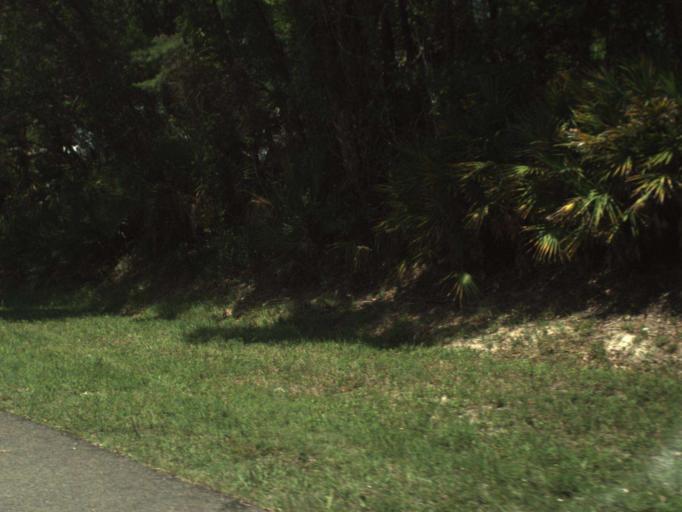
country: US
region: Florida
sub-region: Seminole County
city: Winter Springs
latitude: 28.7079
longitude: -81.3055
